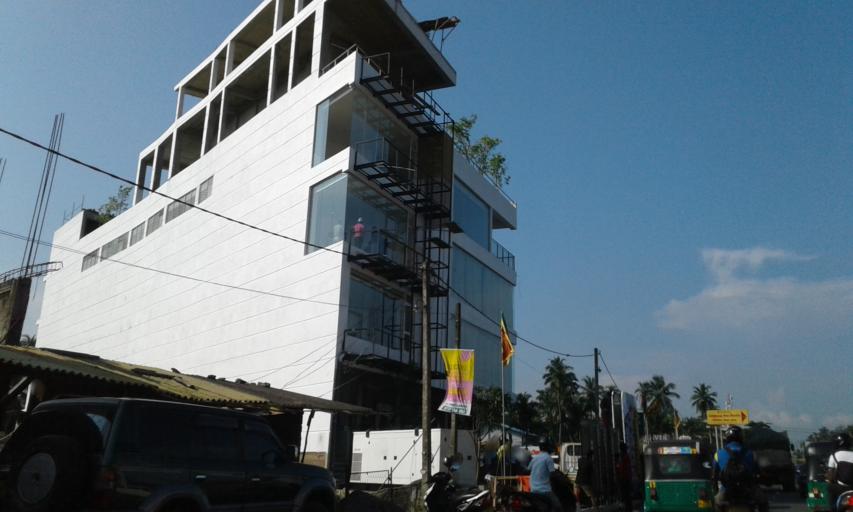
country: LK
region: Western
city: Gampaha
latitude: 7.0254
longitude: 79.9788
